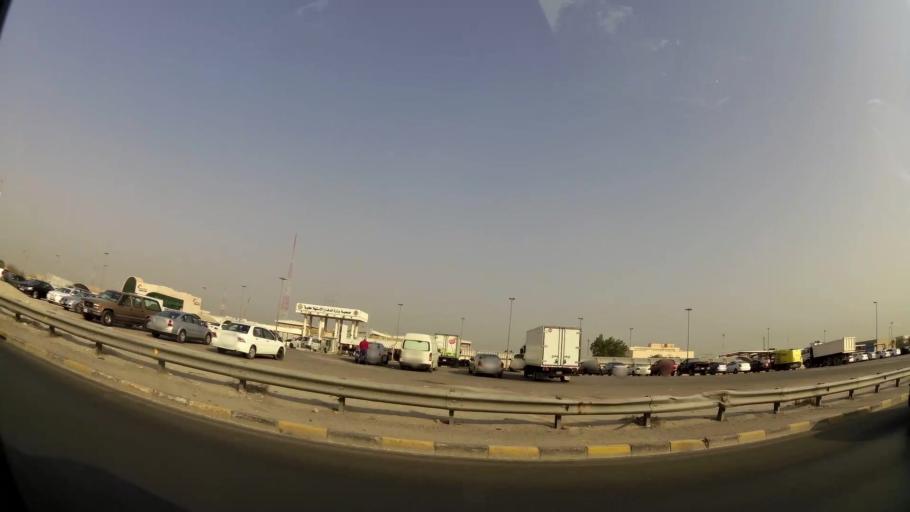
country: KW
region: Al Asimah
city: Ar Rabiyah
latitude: 29.3117
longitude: 47.9197
